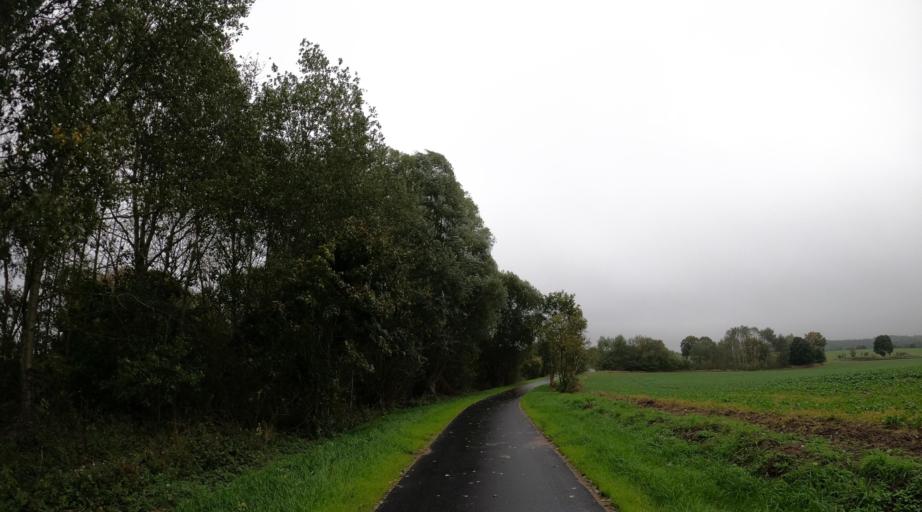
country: PL
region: West Pomeranian Voivodeship
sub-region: Powiat mysliborski
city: Mysliborz
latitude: 52.9213
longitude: 14.7391
